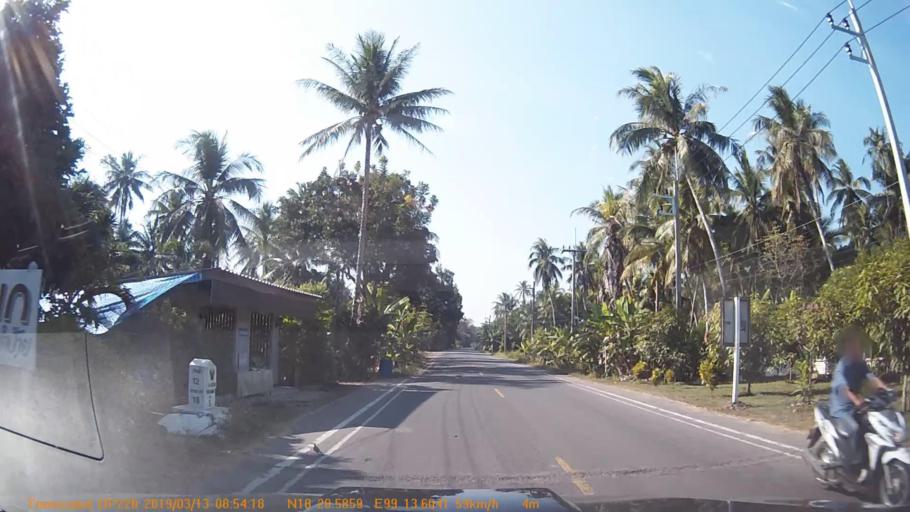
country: TH
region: Chumphon
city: Chumphon
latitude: 10.4762
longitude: 99.2268
